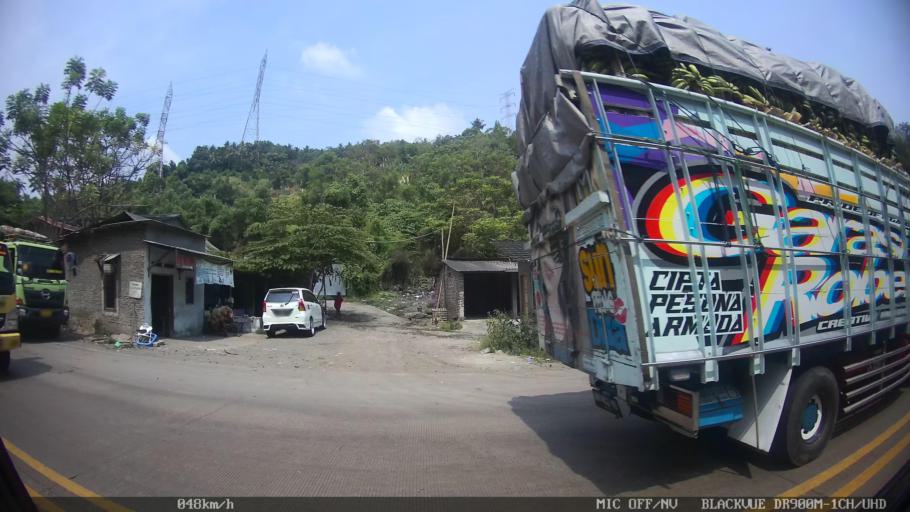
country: ID
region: Banten
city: Curug
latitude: -5.9464
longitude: 106.0041
